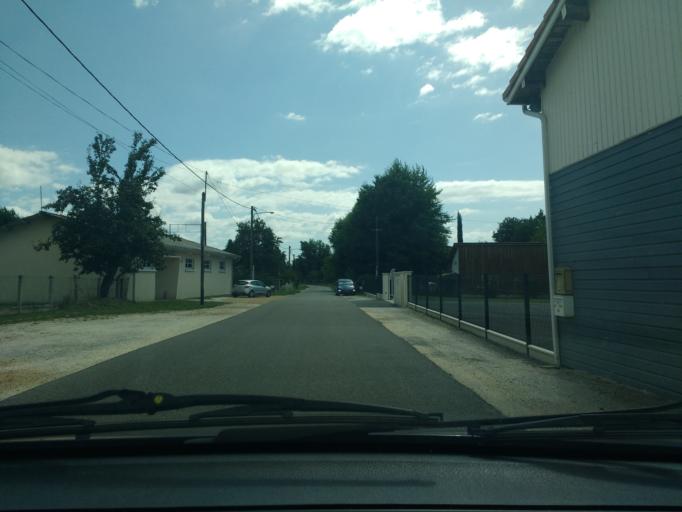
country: FR
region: Aquitaine
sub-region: Departement de la Gironde
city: Salles
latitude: 44.5591
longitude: -0.8556
